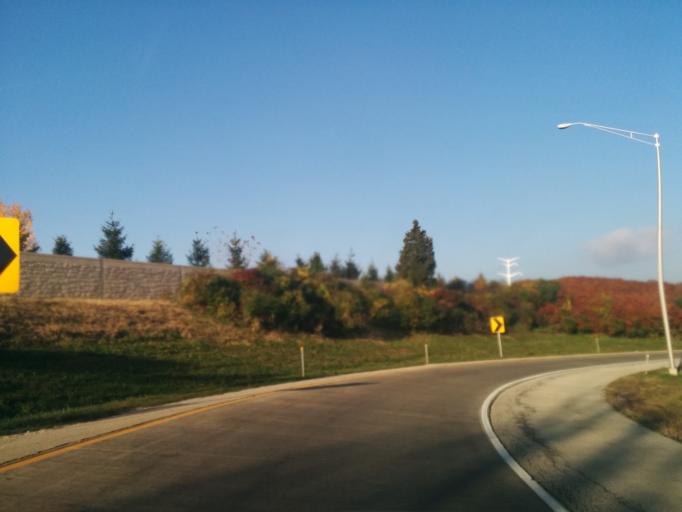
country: US
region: Illinois
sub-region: DuPage County
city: Oakbrook Terrace
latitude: 41.8433
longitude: -87.9585
